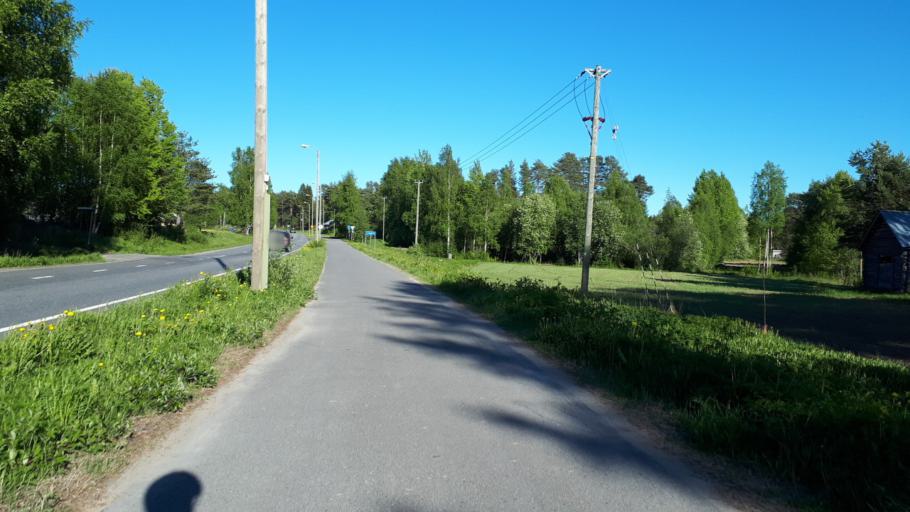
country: FI
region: Northern Ostrobothnia
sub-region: Oulunkaari
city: Ii
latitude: 65.3227
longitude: 25.4536
